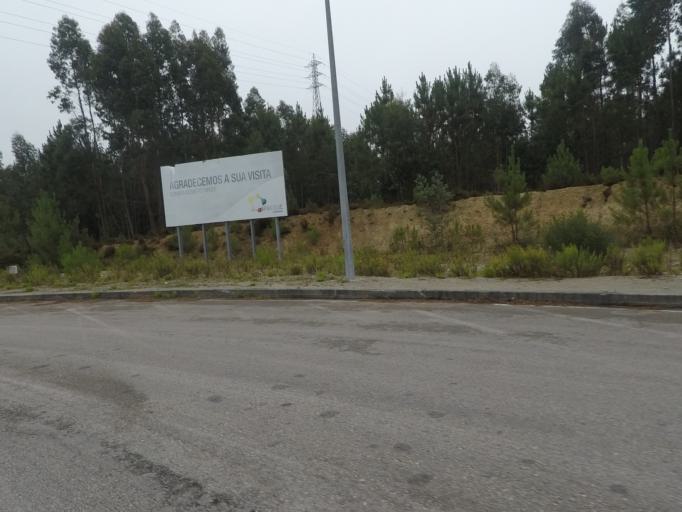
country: PT
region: Coimbra
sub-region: Coimbra
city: Coimbra
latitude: 40.1776
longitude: -8.4626
